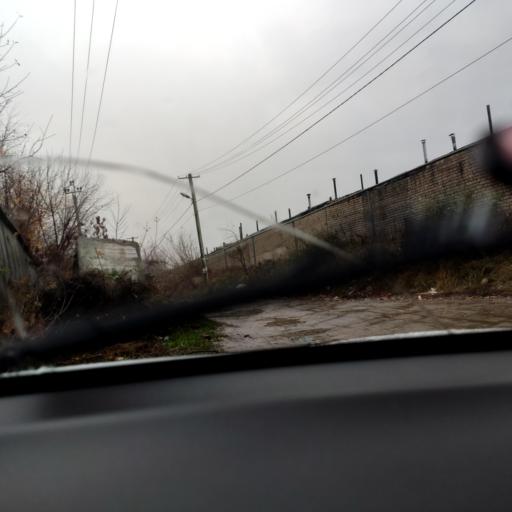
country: RU
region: Tatarstan
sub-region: Gorod Kazan'
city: Kazan
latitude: 55.8683
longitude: 49.1079
